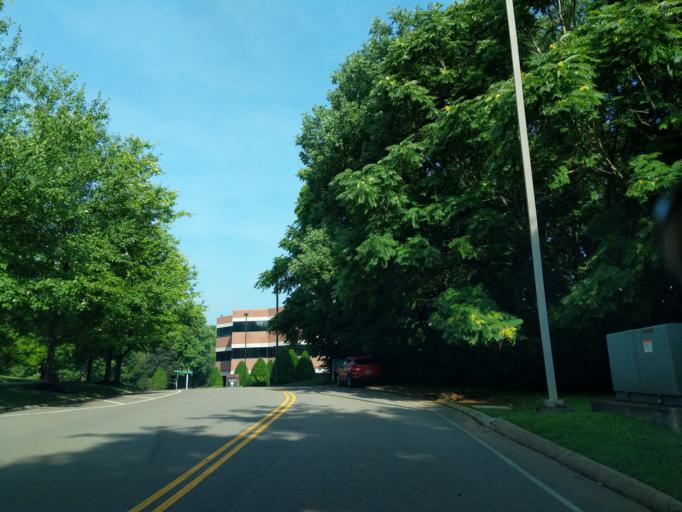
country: US
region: Tennessee
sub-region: Davidson County
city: Goodlettsville
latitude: 36.3098
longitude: -86.6999
